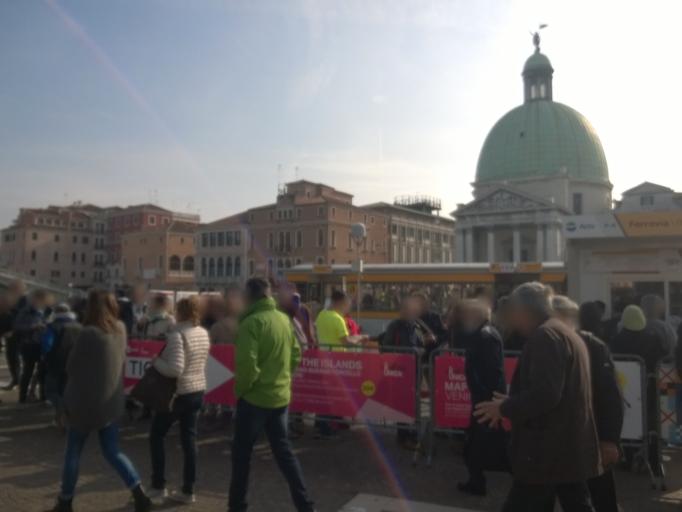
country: IT
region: Veneto
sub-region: Provincia di Venezia
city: Venice
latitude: 45.4408
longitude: 12.3215
